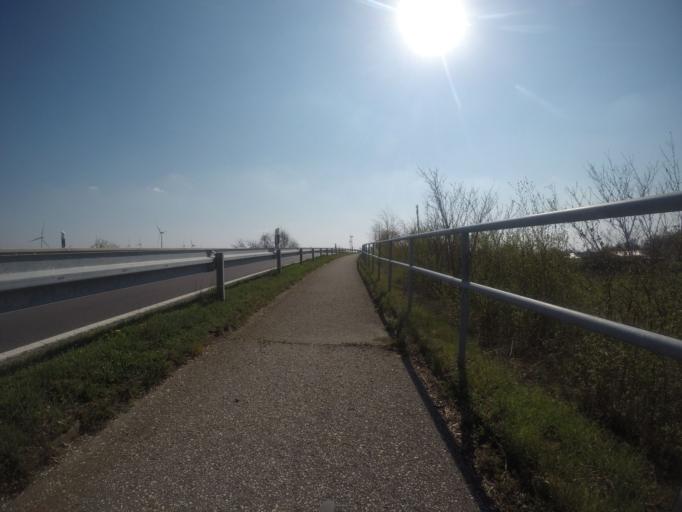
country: DE
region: Brandenburg
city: Nauen
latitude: 52.5591
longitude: 12.8696
